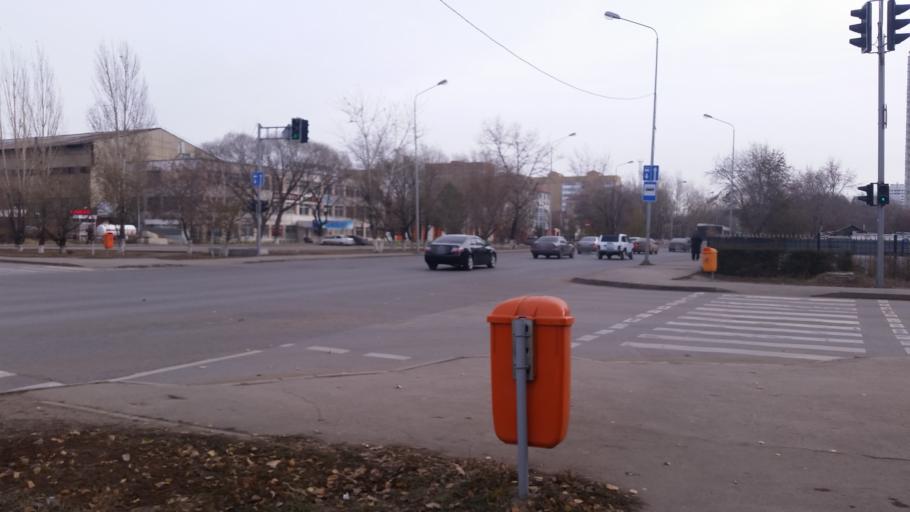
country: KZ
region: Astana Qalasy
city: Astana
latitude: 51.1660
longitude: 71.4629
